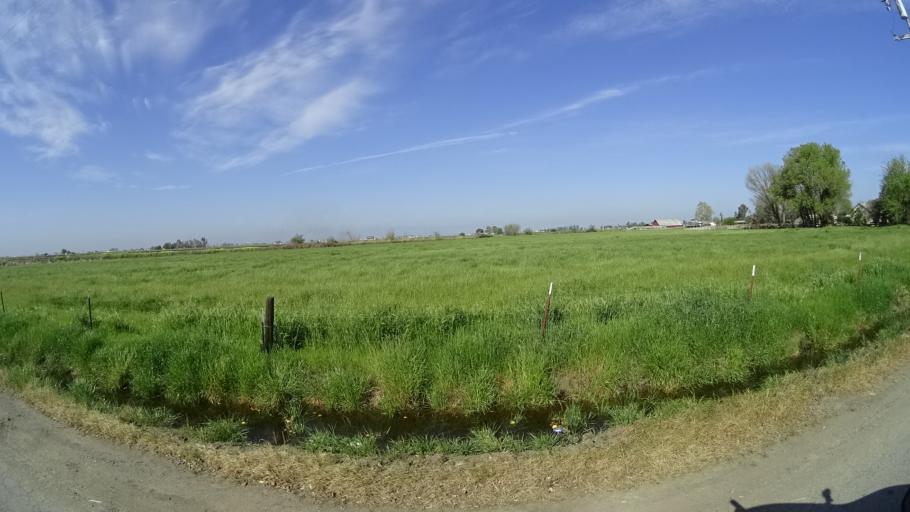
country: US
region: California
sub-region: Glenn County
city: Willows
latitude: 39.5769
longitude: -122.0371
